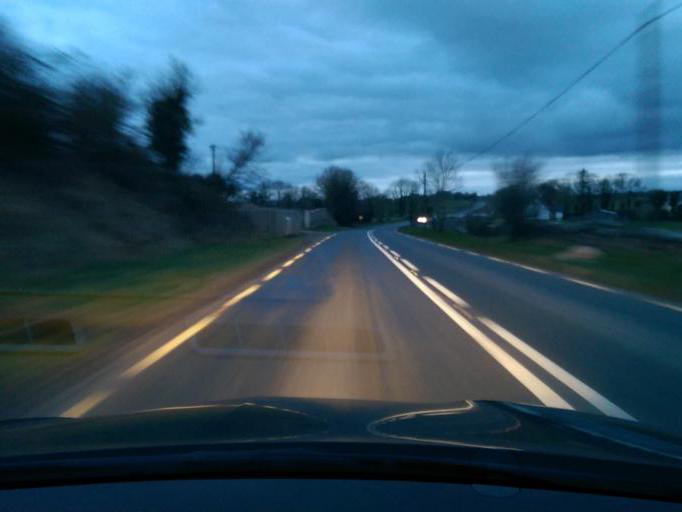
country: IE
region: Connaught
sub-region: County Galway
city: Loughrea
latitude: 53.1911
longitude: -8.3806
